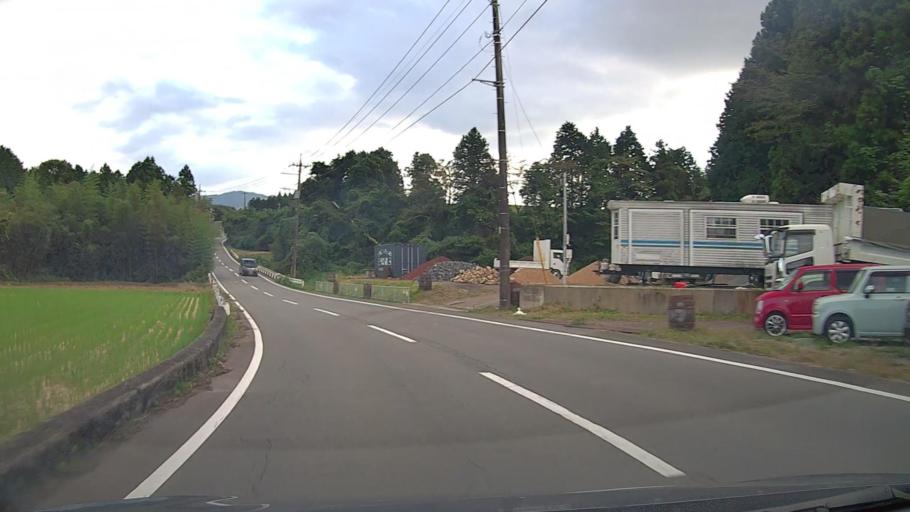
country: JP
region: Shizuoka
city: Gotemba
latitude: 35.3286
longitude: 138.9612
